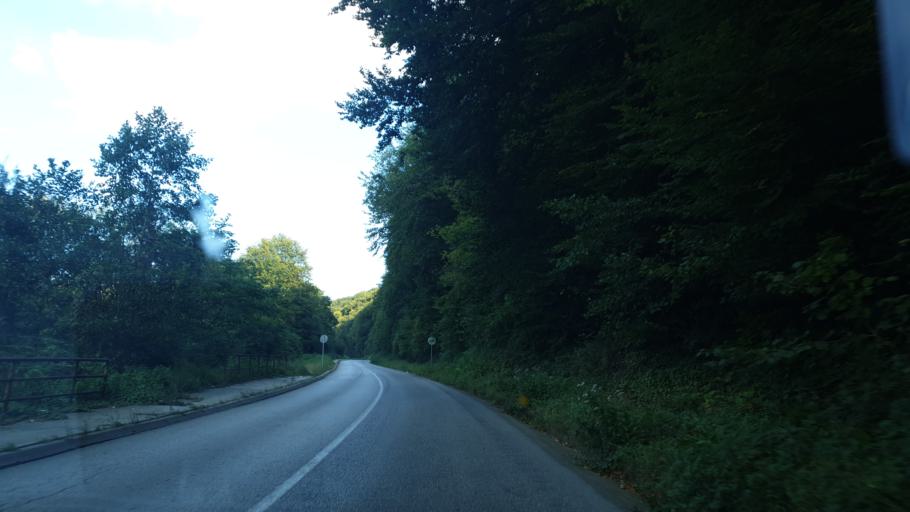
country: RS
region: Central Serbia
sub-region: Zlatiborski Okrug
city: Uzice
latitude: 43.8581
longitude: 19.8666
